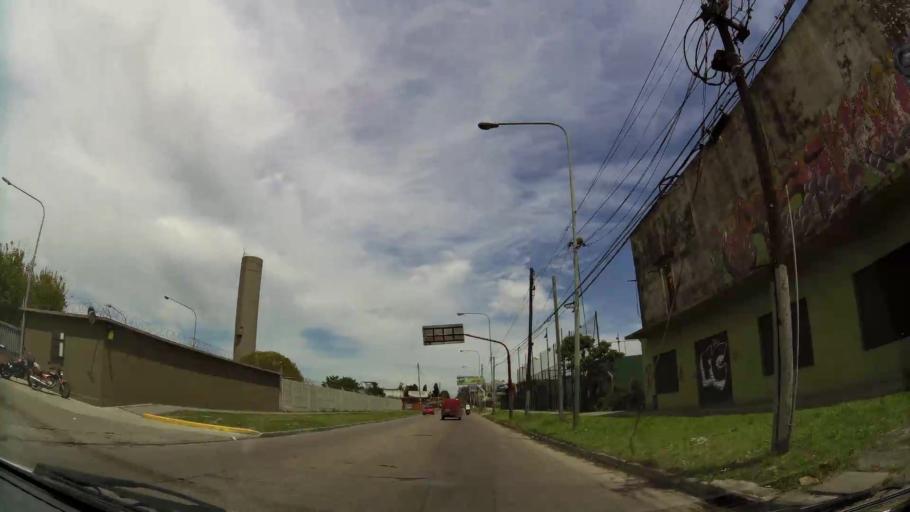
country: AR
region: Buenos Aires
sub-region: Partido de Quilmes
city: Quilmes
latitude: -34.7763
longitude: -58.2544
